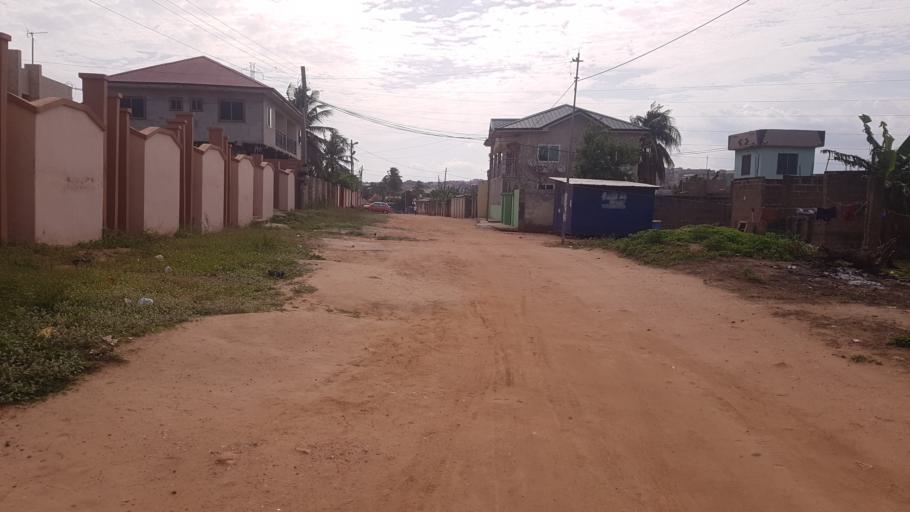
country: GH
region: Greater Accra
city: Gbawe
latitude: 5.5511
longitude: -0.3421
